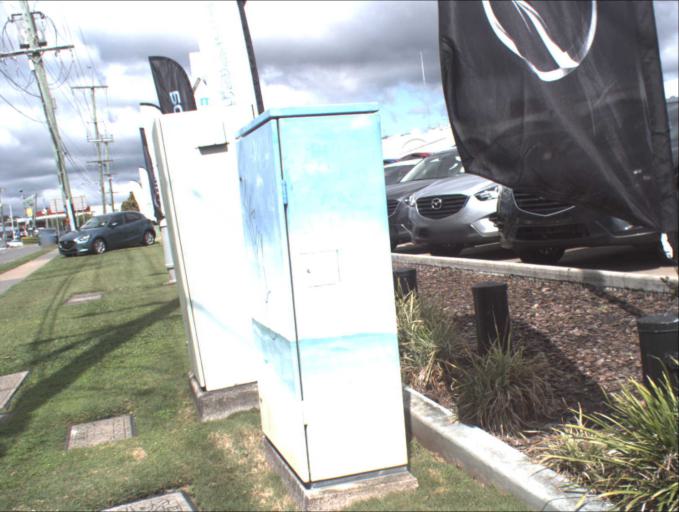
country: AU
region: Queensland
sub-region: Logan
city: Park Ridge South
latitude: -27.6675
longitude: 153.0327
